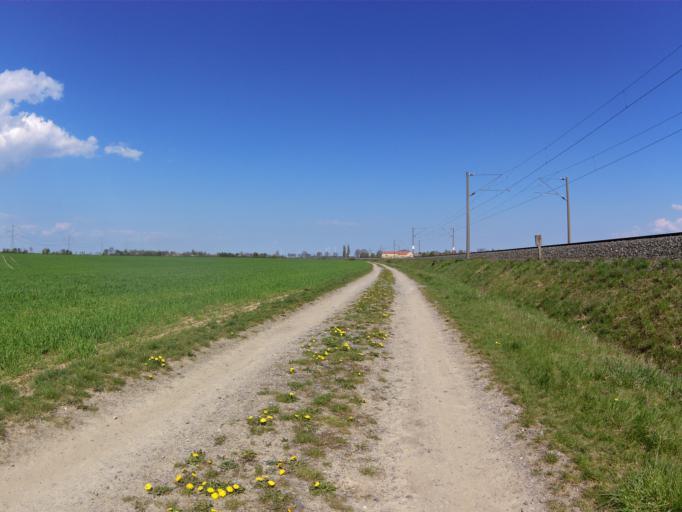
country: DE
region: Bavaria
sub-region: Regierungsbezirk Unterfranken
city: Oberpleichfeld
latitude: 49.8376
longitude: 10.0981
